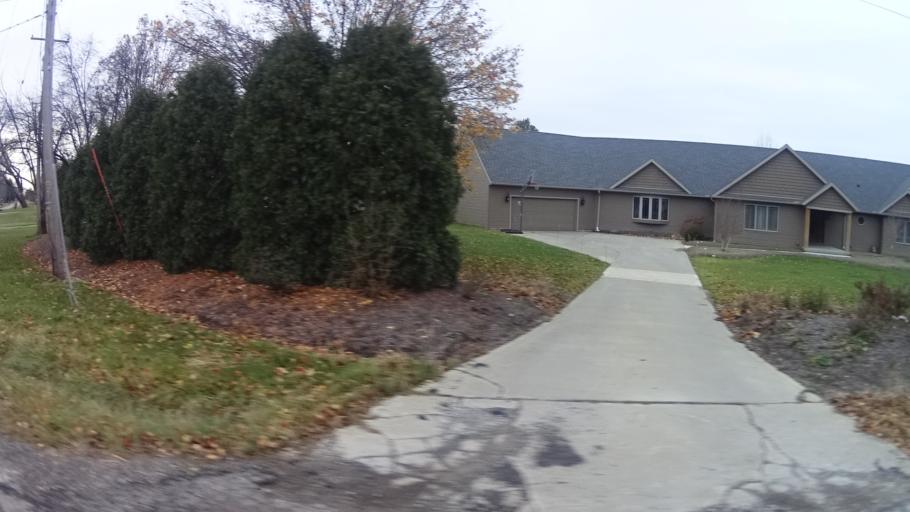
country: US
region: Ohio
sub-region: Lorain County
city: Eaton Estates
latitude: 41.3438
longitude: -81.9714
